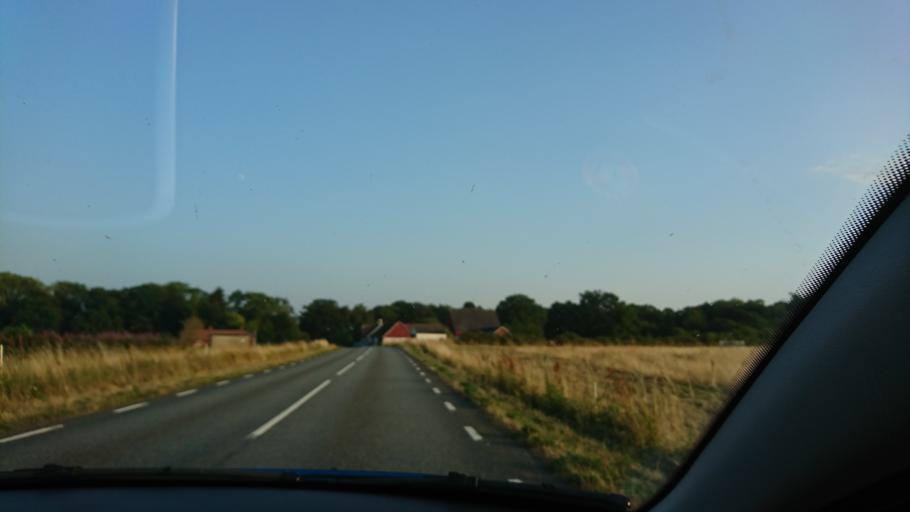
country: SE
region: Skane
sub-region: Simrishamns Kommun
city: Kivik
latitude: 55.7026
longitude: 14.1505
